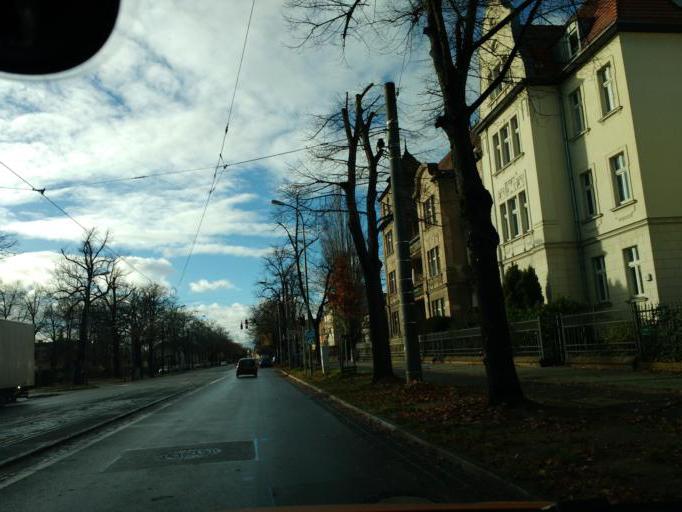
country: DE
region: Brandenburg
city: Potsdam
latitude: 52.4121
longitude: 13.0847
